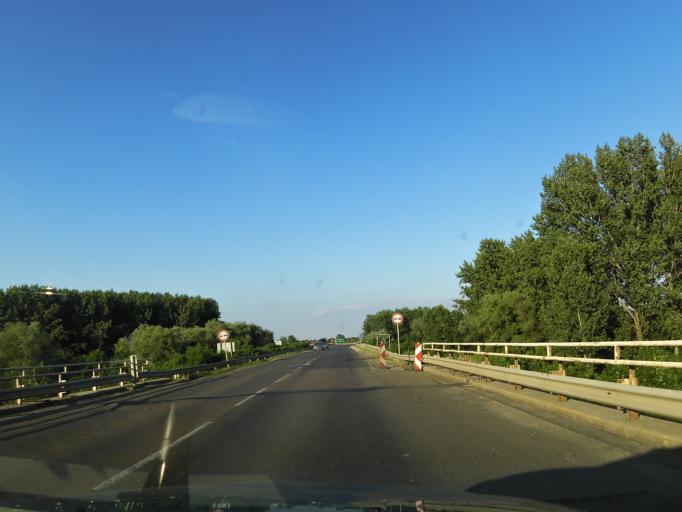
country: HU
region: Jasz-Nagykun-Szolnok
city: Kunszentmarton
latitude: 46.8486
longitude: 20.2745
